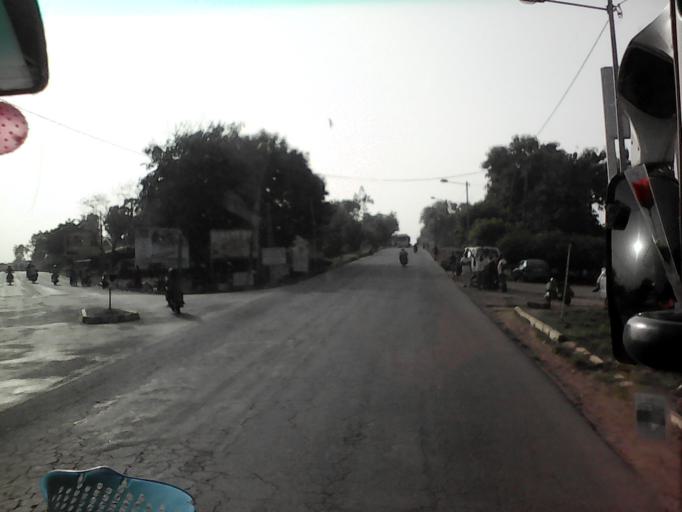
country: TG
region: Kara
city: Kara
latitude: 9.5317
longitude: 1.2016
